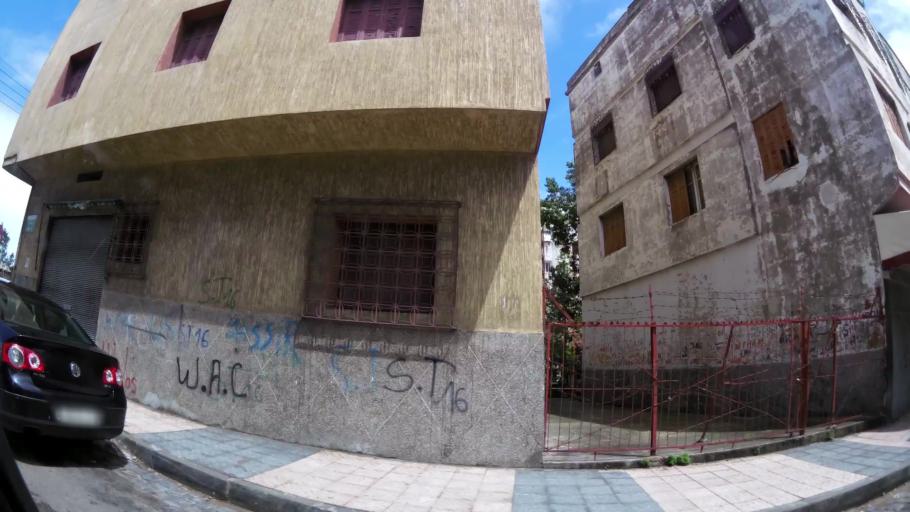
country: MA
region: Grand Casablanca
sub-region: Casablanca
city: Casablanca
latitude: 33.5738
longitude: -7.5839
